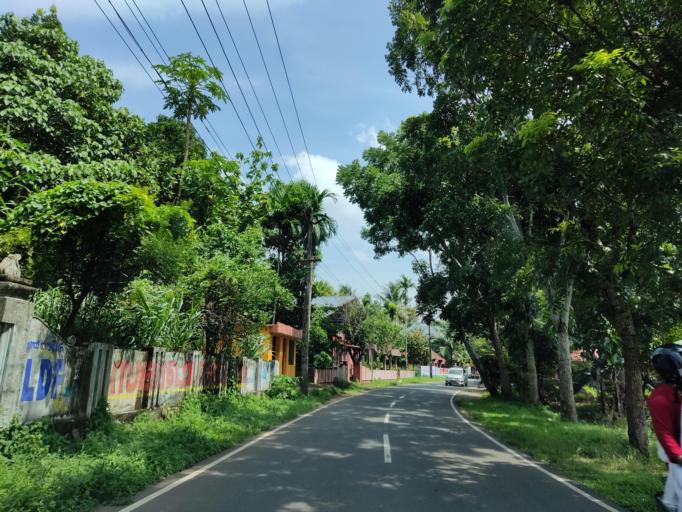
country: IN
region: Kerala
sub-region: Alappuzha
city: Mavelikara
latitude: 9.2879
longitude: 76.5711
